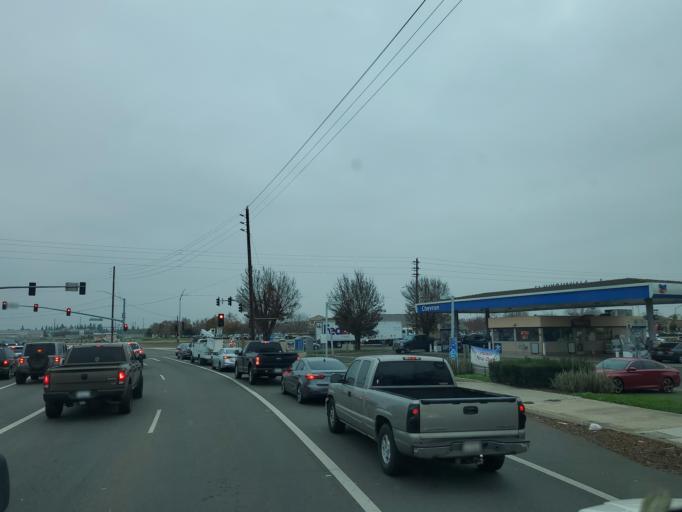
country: US
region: California
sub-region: Stanislaus County
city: Salida
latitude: 37.6994
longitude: -121.0689
